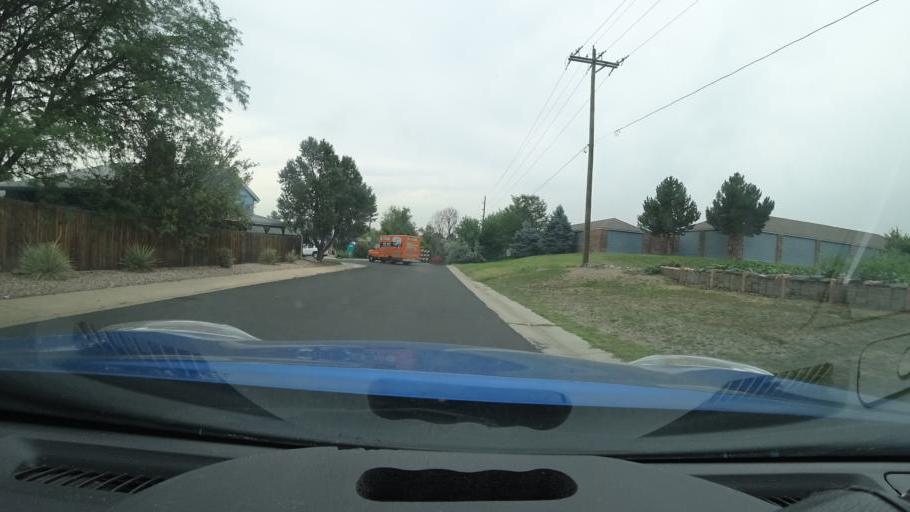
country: US
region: Colorado
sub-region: Arapahoe County
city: Glendale
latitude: 39.6803
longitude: -104.9058
